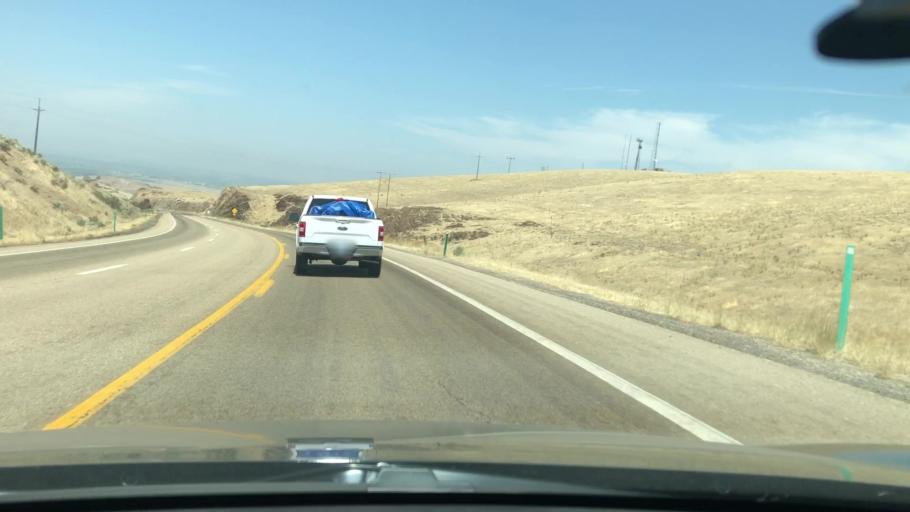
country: US
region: Idaho
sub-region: Owyhee County
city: Marsing
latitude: 43.4212
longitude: -116.8569
